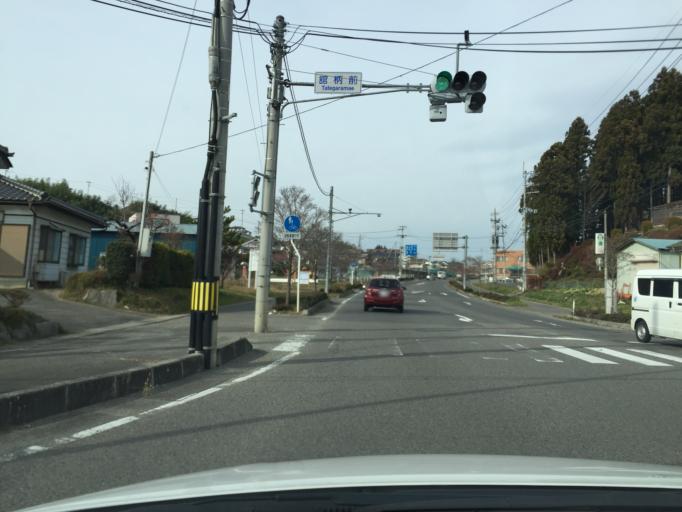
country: JP
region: Fukushima
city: Funehikimachi-funehiki
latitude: 37.4363
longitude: 140.5913
